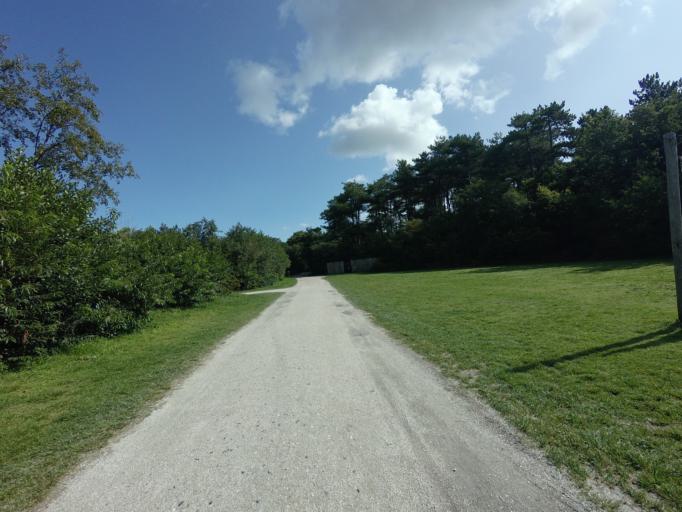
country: NL
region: Friesland
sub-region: Gemeente Terschelling
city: West-Terschelling
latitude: 53.3700
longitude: 5.2145
